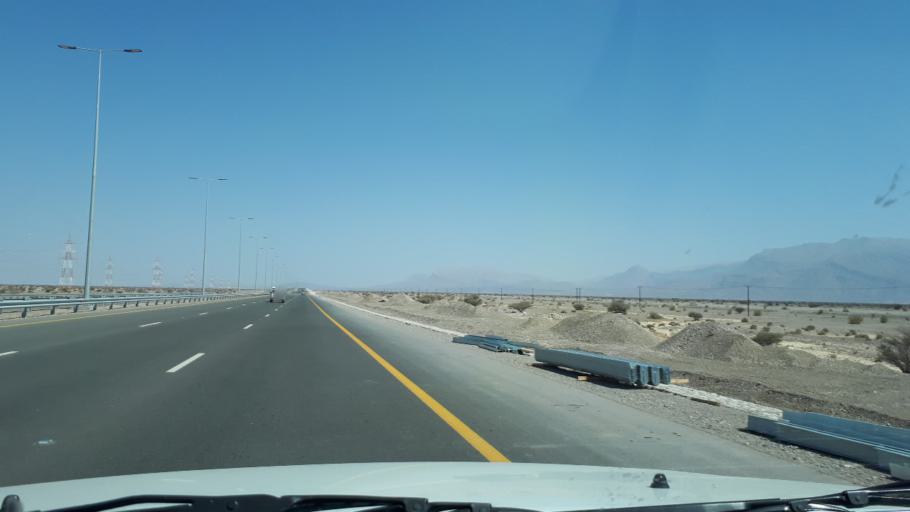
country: OM
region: Ash Sharqiyah
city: Badiyah
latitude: 22.3078
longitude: 59.1427
